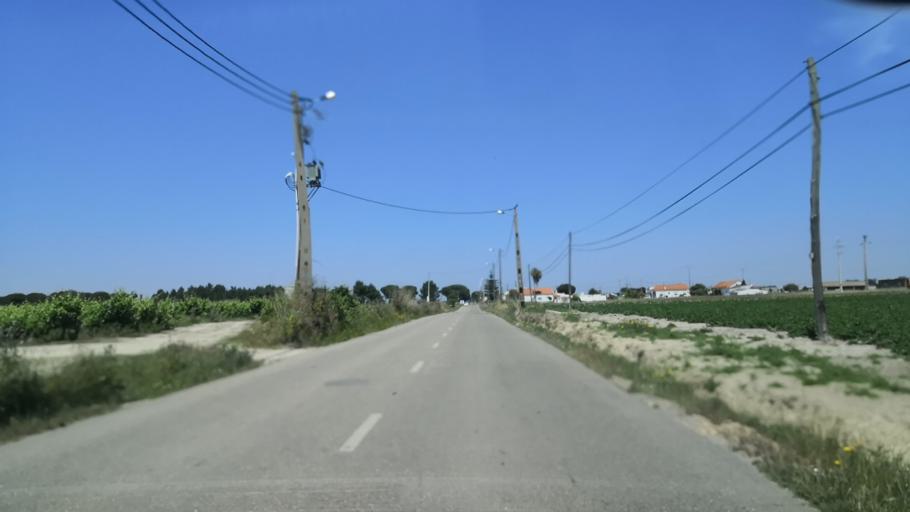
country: PT
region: Santarem
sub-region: Benavente
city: Poceirao
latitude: 38.6719
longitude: -8.7354
